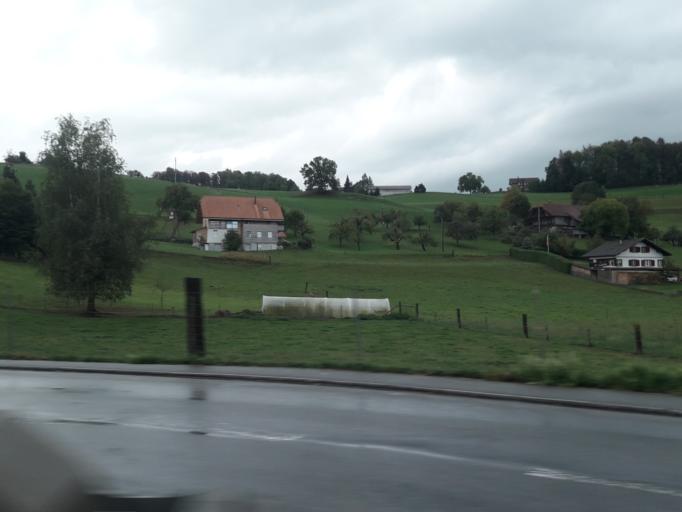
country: CH
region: Bern
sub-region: Thun District
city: Seftigen
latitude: 46.7868
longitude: 7.5418
